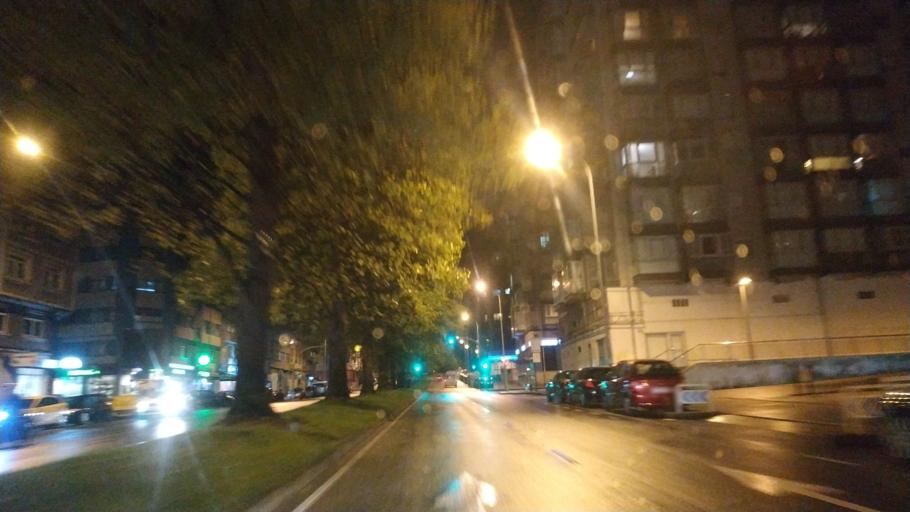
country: ES
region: Galicia
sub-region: Provincia da Coruna
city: A Coruna
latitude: 43.3556
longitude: -8.4138
